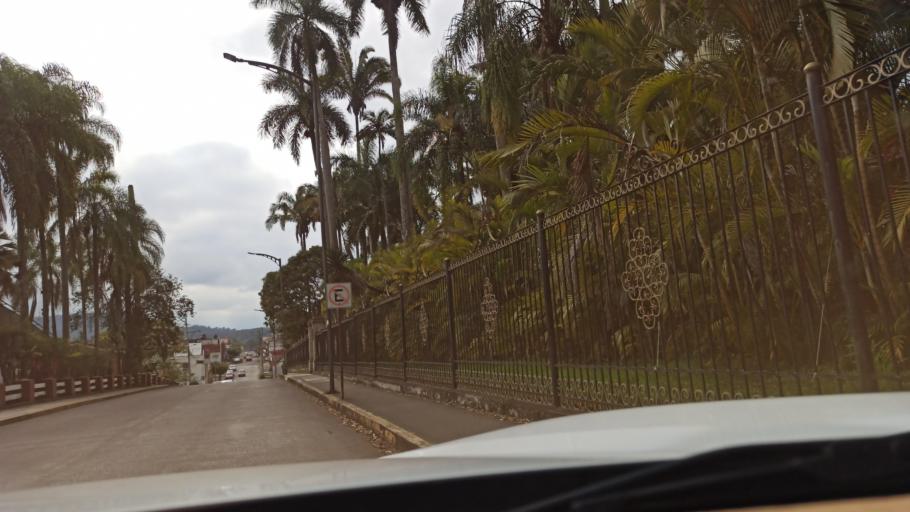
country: MX
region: Veracruz
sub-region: Fortin
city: Fortin de las Flores
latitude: 18.9058
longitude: -96.9972
